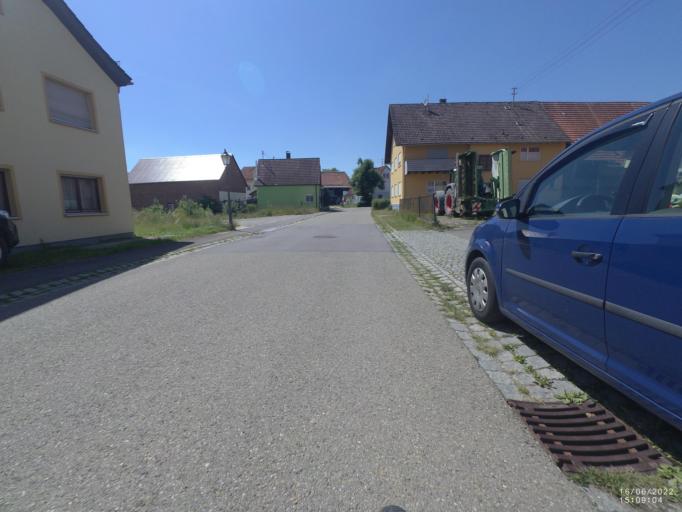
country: DE
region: Baden-Wuerttemberg
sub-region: Regierungsbezirk Stuttgart
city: Gerstetten
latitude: 48.6045
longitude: 10.0667
